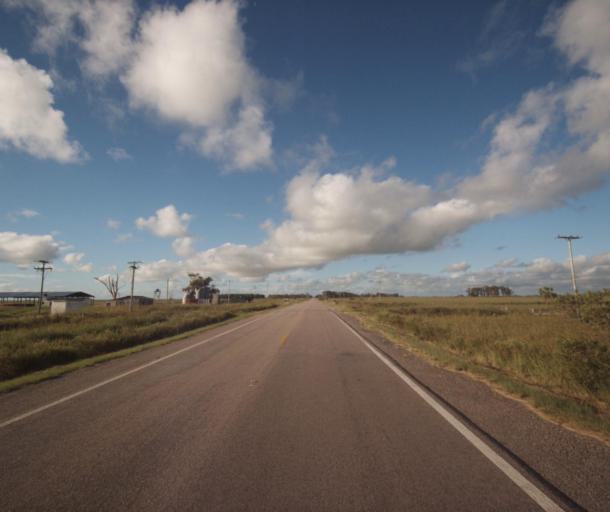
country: BR
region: Rio Grande do Sul
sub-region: Arroio Grande
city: Arroio Grande
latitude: -32.3814
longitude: -52.5533
